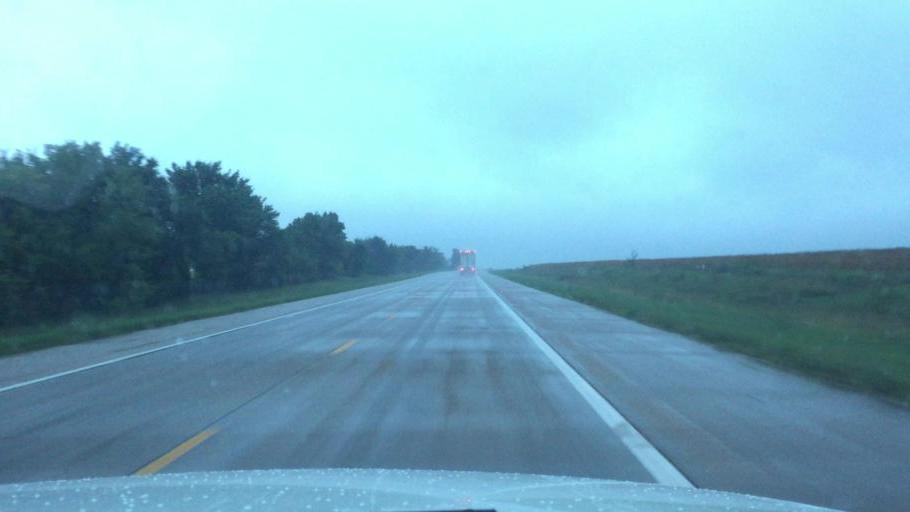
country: US
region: Kansas
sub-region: Neosho County
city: Chanute
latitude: 37.5398
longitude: -95.4707
